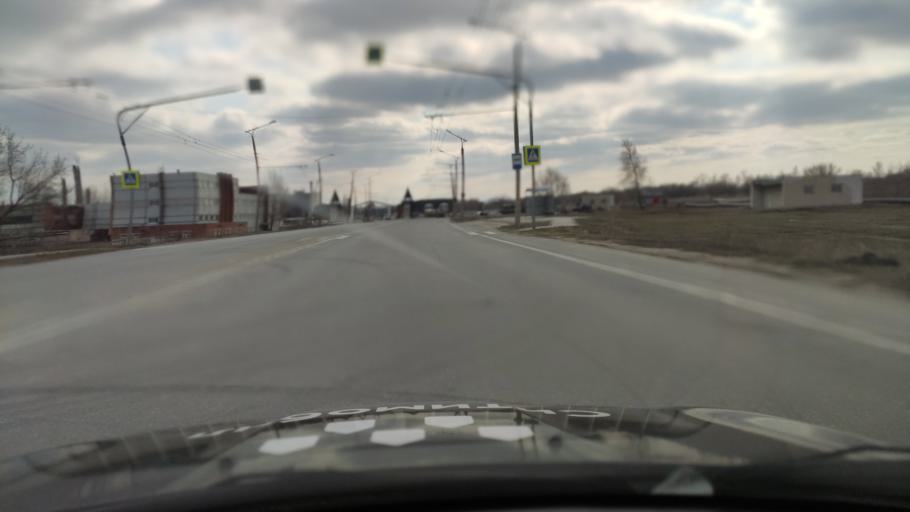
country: RU
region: Samara
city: Povolzhskiy
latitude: 53.5465
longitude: 49.6026
